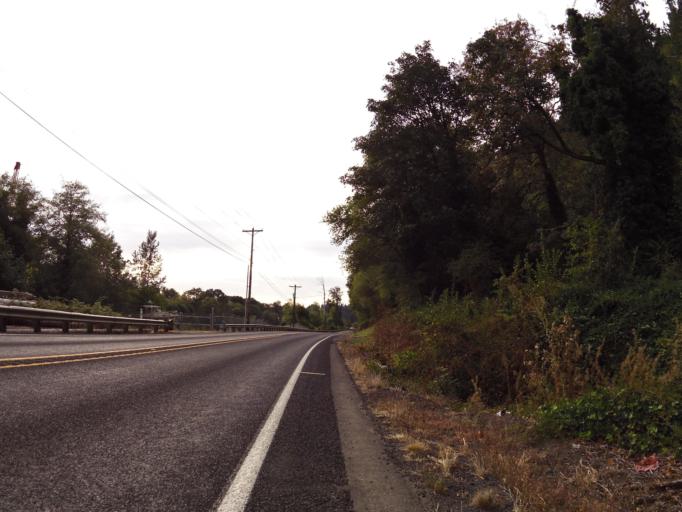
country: US
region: Washington
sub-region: Cowlitz County
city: West Longview
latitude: 46.1884
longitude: -123.1001
